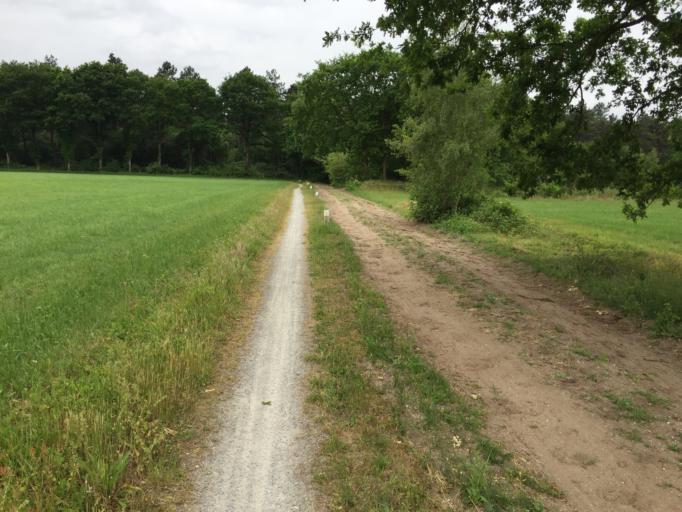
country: NL
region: Drenthe
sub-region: Gemeente Tynaarlo
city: Vries
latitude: 53.0810
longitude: 6.5170
